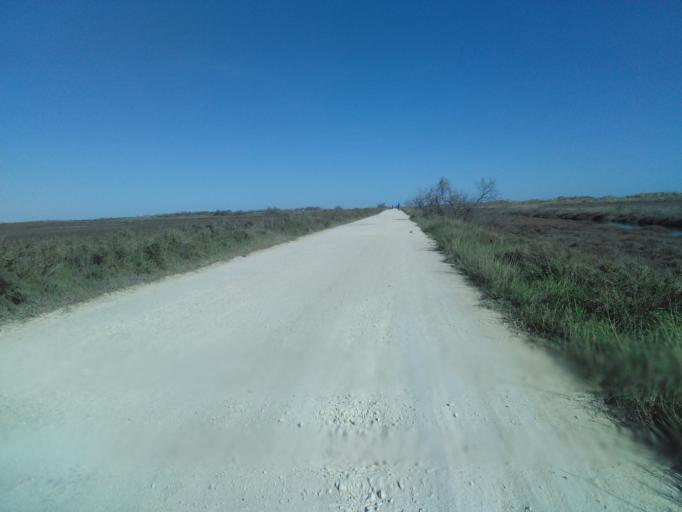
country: FR
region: Provence-Alpes-Cote d'Azur
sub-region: Departement des Bouches-du-Rhone
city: Saintes-Maries-de-la-Mer
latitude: 43.4607
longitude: 4.4872
